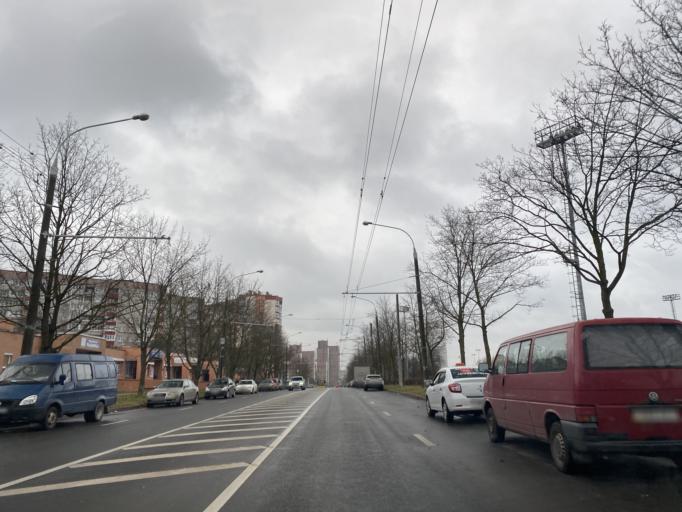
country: BY
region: Minsk
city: Bal'shavik
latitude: 53.9567
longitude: 27.6099
